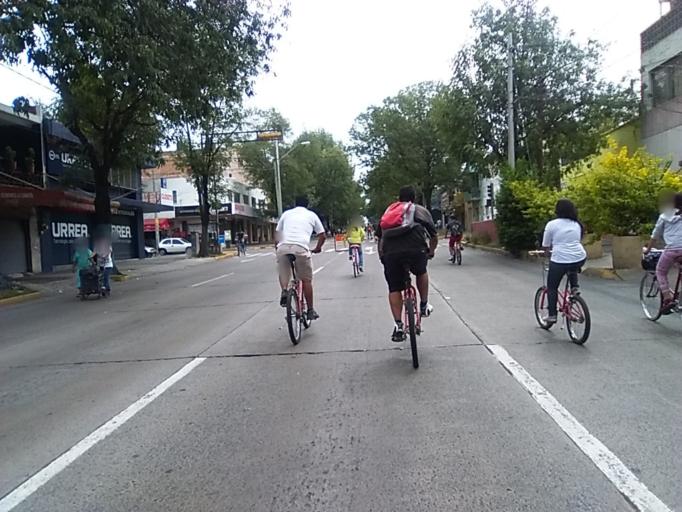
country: MX
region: Jalisco
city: Tlaquepaque
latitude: 20.6715
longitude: -103.3271
